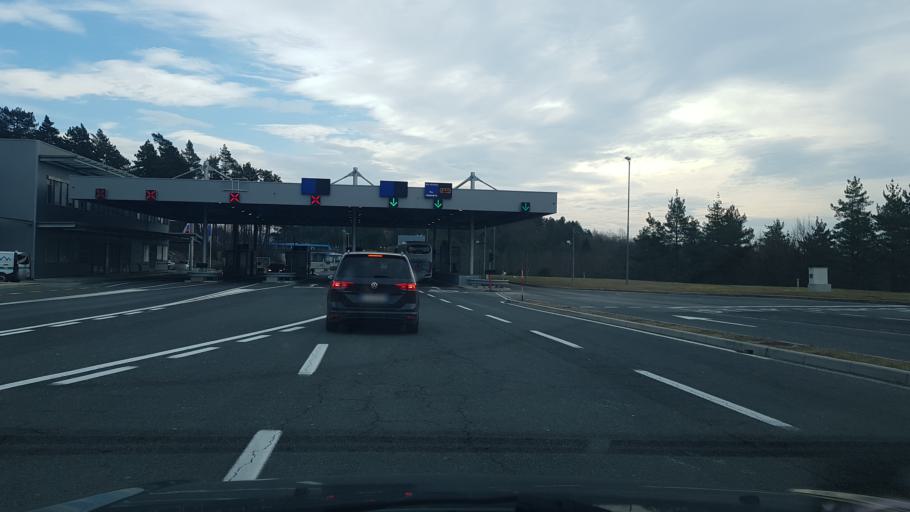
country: SI
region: Ilirska Bistrica
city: Ilirska Bistrica
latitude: 45.4921
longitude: 14.2120
